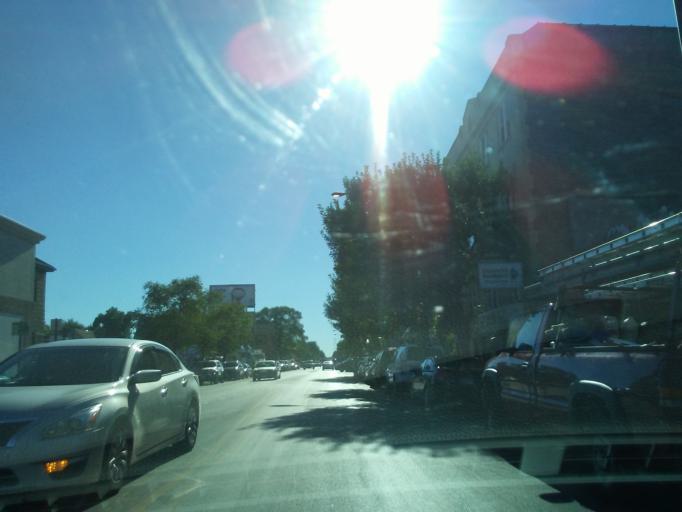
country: US
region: Illinois
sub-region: Cook County
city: Oak Park
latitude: 41.9171
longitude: -87.7364
